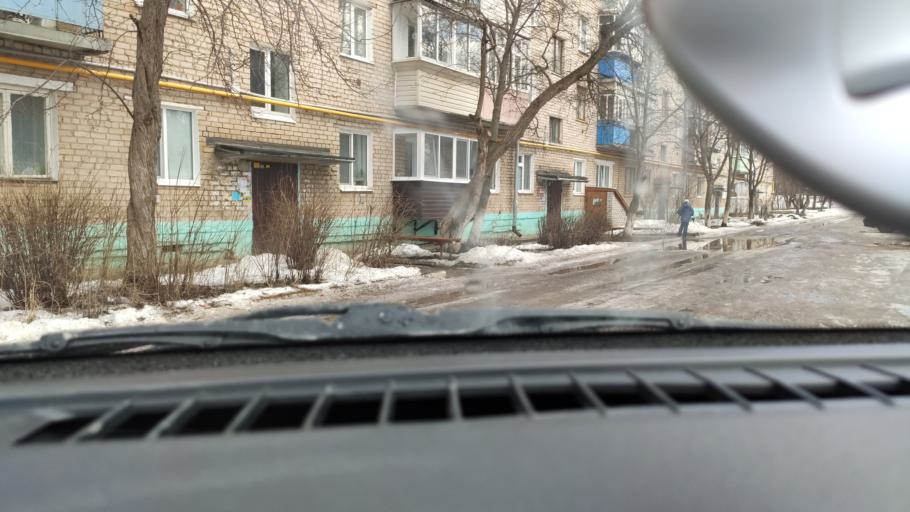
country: RU
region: Perm
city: Nytva
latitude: 57.9306
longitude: 55.3073
